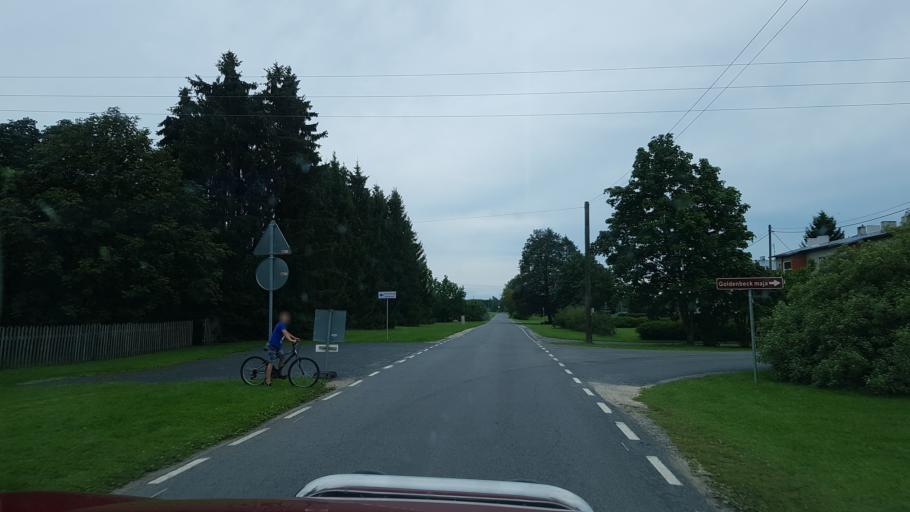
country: EE
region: Harju
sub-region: Nissi vald
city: Turba
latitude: 58.8787
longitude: 24.0783
